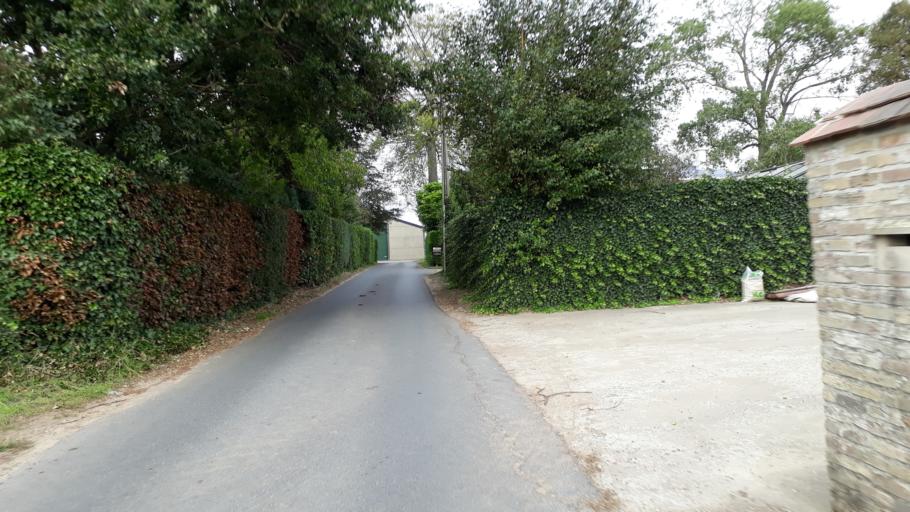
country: BE
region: Flanders
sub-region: Provincie West-Vlaanderen
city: Lichtervelde
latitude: 51.0556
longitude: 3.1358
